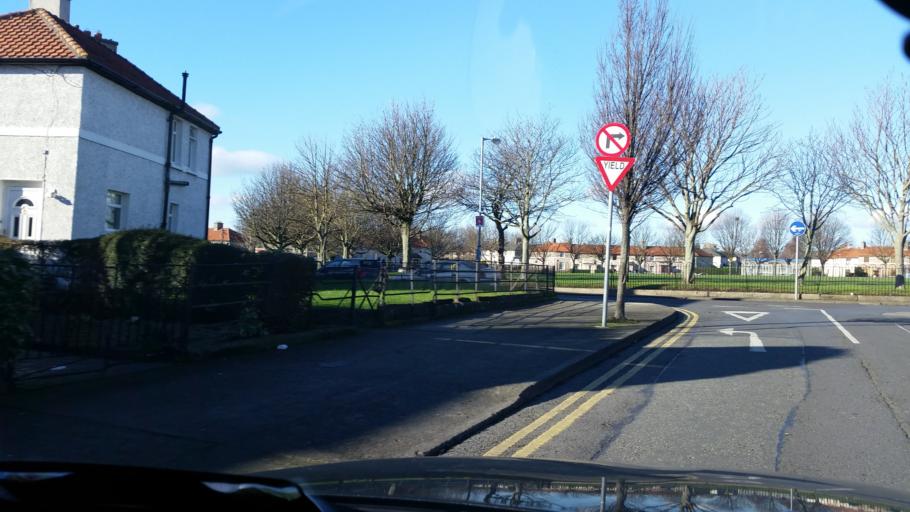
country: IE
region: Leinster
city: Marino
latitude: 53.3657
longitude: -6.2335
